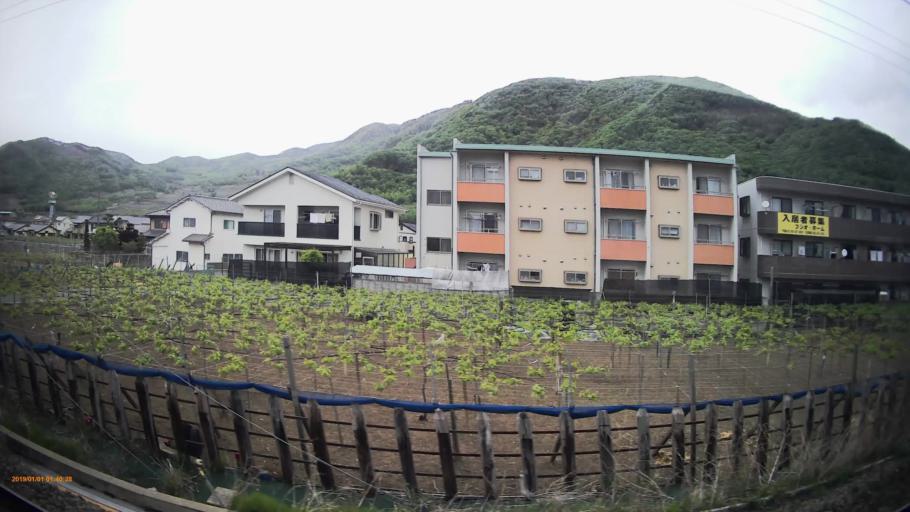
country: JP
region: Yamanashi
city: Isawa
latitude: 35.6570
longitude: 138.6211
